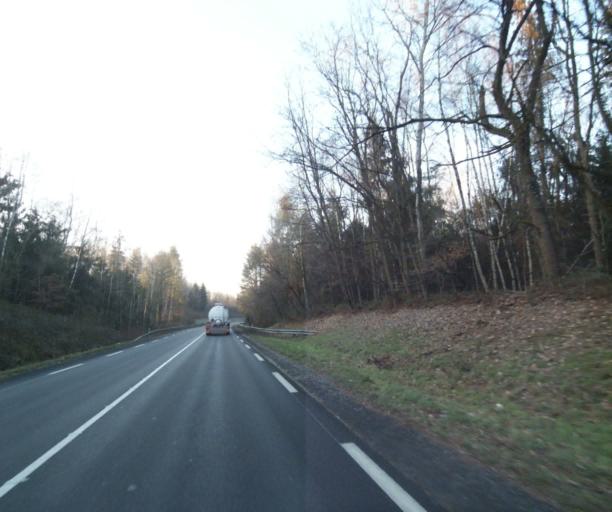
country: FR
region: Champagne-Ardenne
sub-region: Departement de la Haute-Marne
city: Bienville
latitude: 48.5639
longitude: 5.0387
